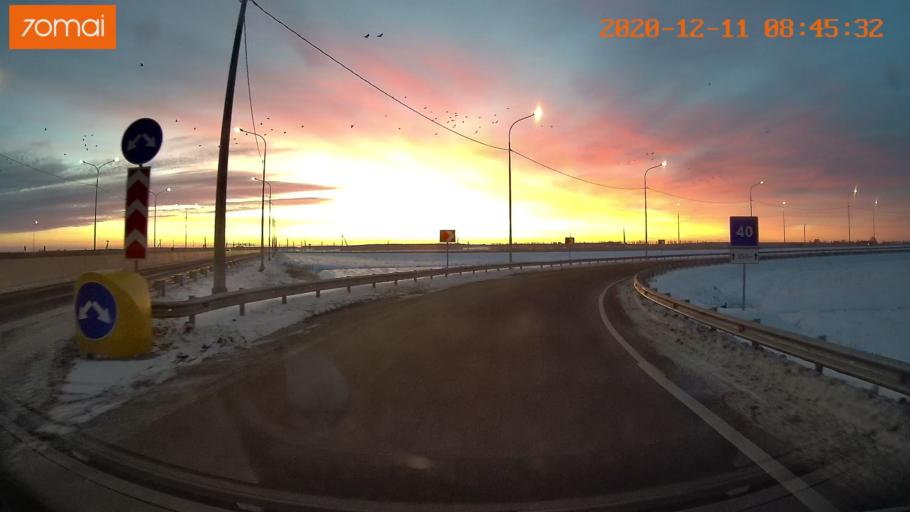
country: RU
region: Vologda
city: Vologda
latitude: 59.1570
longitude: 39.8141
